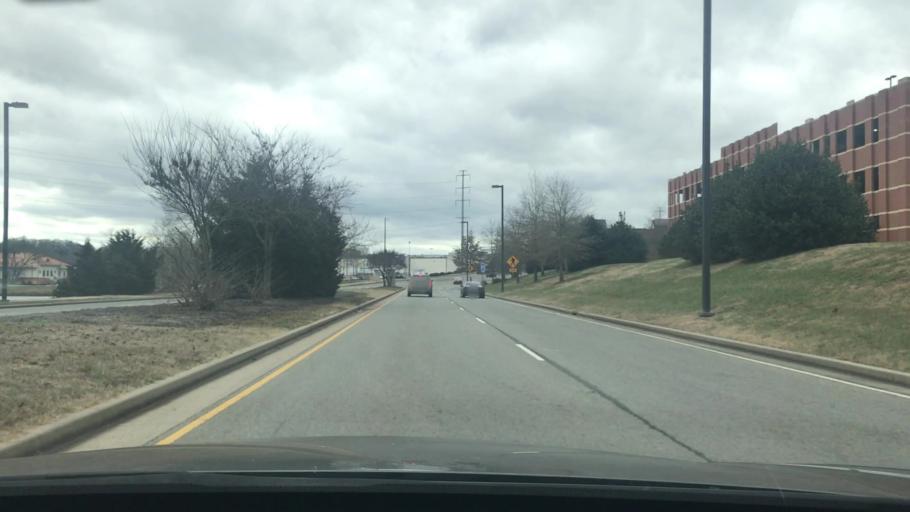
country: US
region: Tennessee
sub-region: Williamson County
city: Franklin
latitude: 35.9170
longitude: -86.8170
